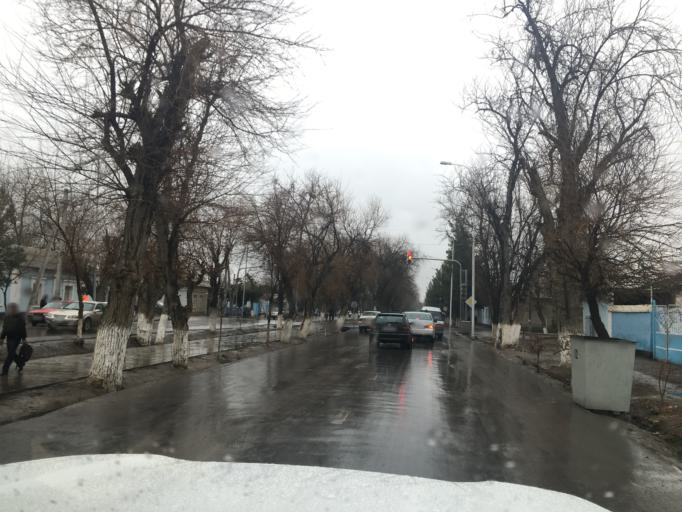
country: TM
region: Mary
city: Yoloeten
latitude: 37.2959
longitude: 62.3616
